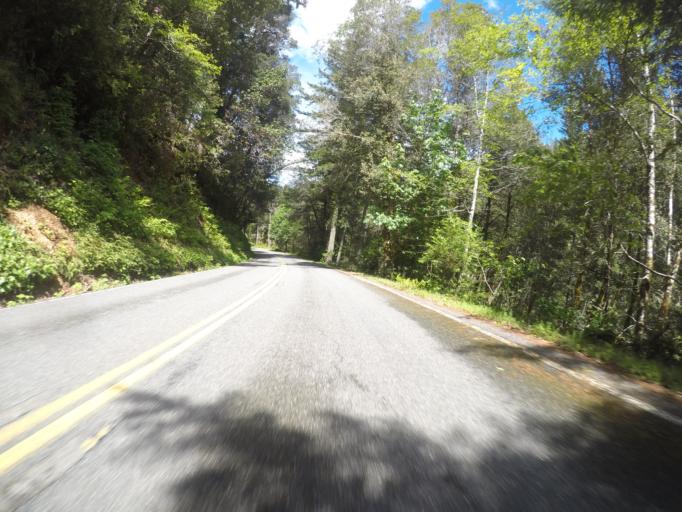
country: US
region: California
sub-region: Del Norte County
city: Bertsch-Oceanview
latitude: 41.7967
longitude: -124.0502
